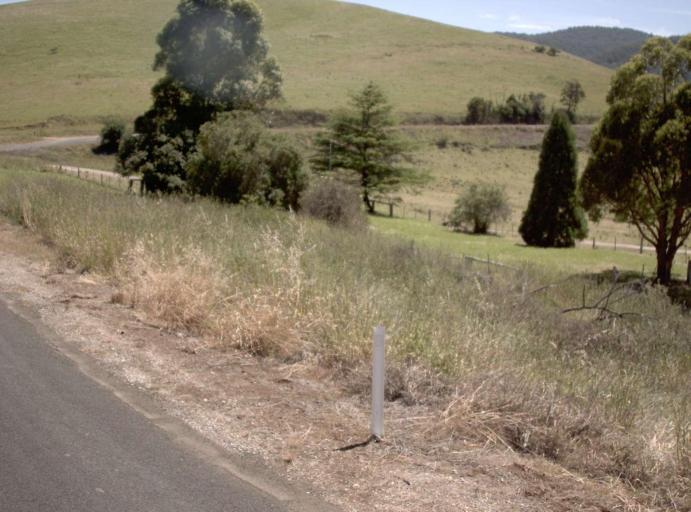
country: AU
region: Victoria
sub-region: East Gippsland
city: Lakes Entrance
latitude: -37.4141
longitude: 148.2051
